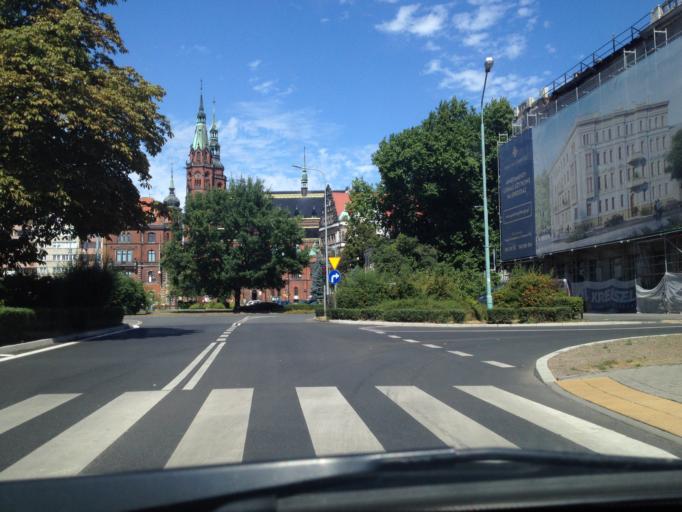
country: PL
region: Lower Silesian Voivodeship
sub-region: Legnica
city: Legnica
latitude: 51.2052
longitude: 16.1631
